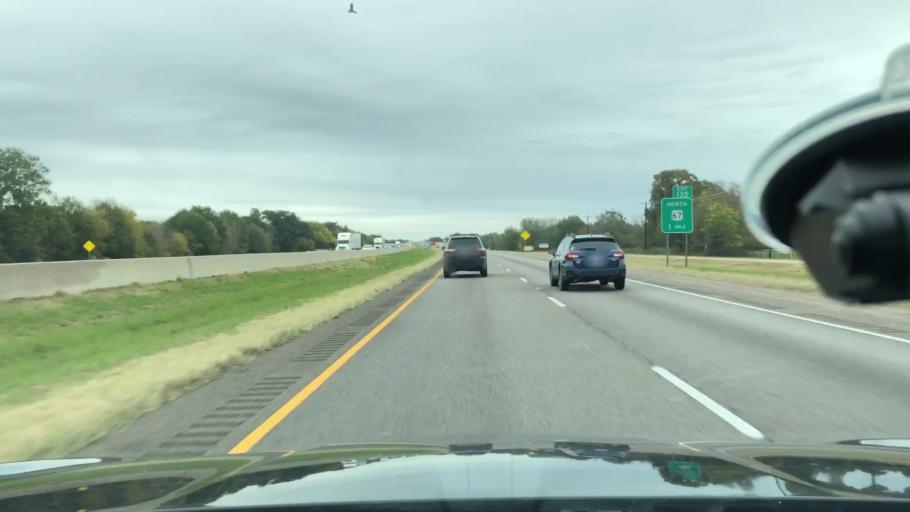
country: US
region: Texas
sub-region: Hopkins County
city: Sulphur Springs
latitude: 33.1484
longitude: -95.4468
